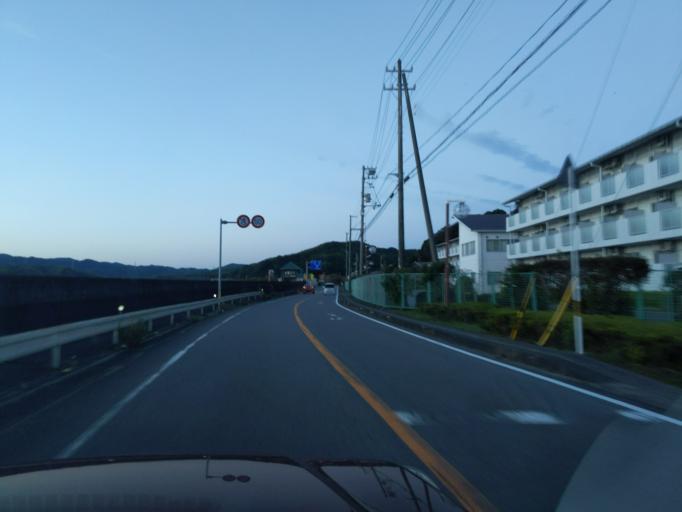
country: JP
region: Tokushima
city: Anan
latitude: 33.8631
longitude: 134.6314
